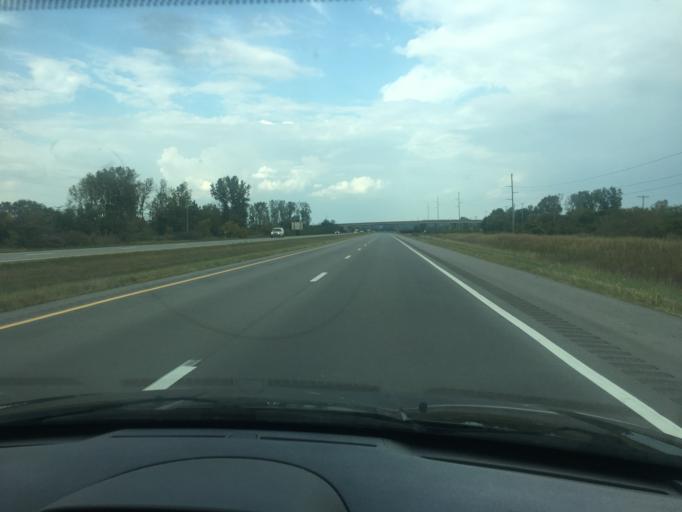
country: US
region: Ohio
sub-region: Clark County
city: Springfield
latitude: 39.9548
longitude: -83.8298
